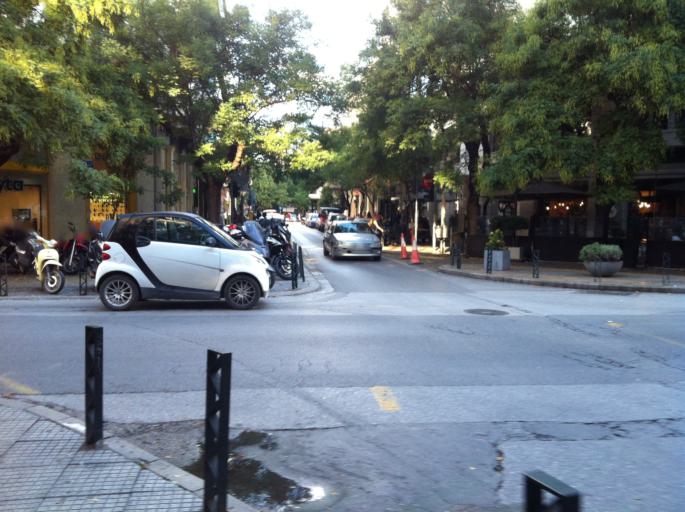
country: GR
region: Central Macedonia
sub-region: Nomos Thessalonikis
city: Thessaloniki
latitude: 40.6335
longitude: 22.9398
